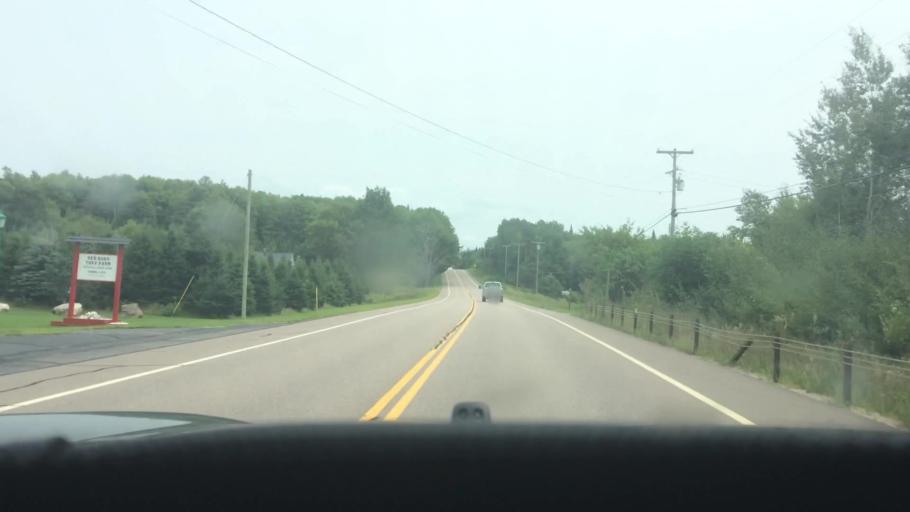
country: US
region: New York
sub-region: Franklin County
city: Malone
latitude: 44.8530
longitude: -74.0769
